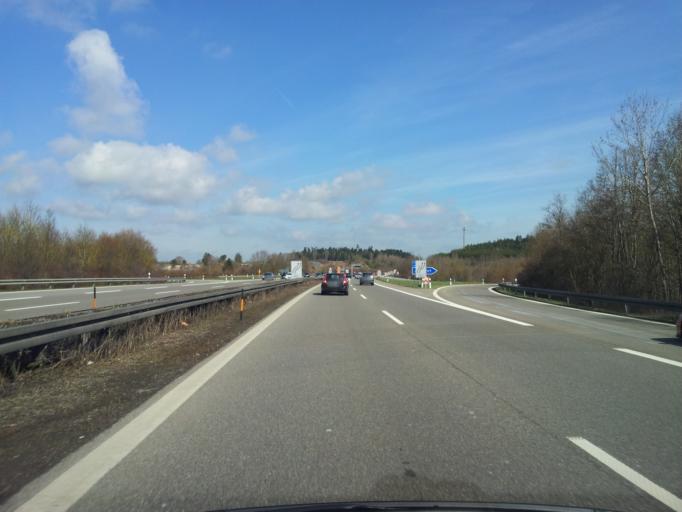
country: DE
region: Baden-Wuerttemberg
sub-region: Freiburg Region
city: Vohringen
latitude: 48.2961
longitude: 8.6351
